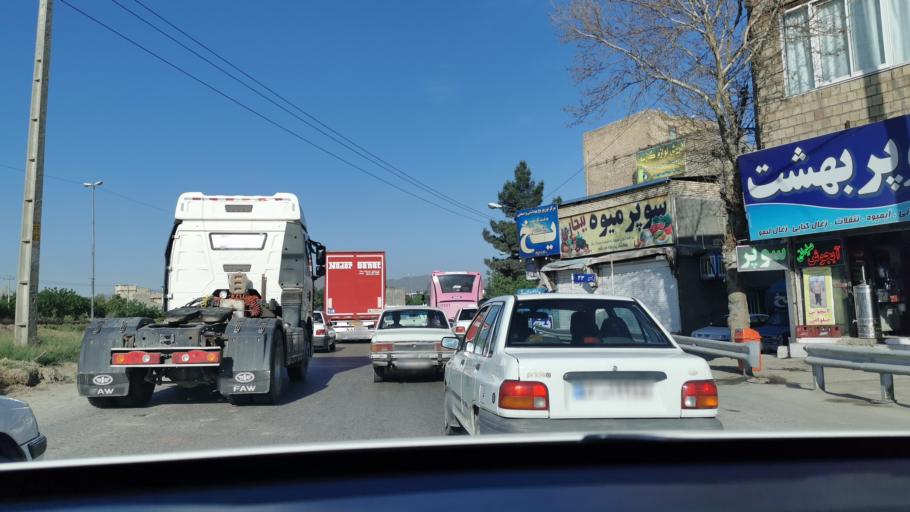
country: IR
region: Razavi Khorasan
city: Mashhad
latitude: 36.2595
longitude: 59.6425
